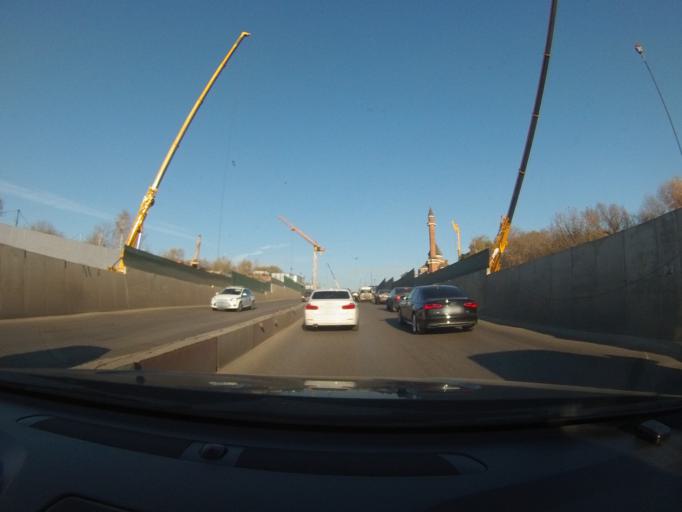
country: RU
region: Moskovskaya
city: Kastanayevo
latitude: 55.7236
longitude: 37.4979
